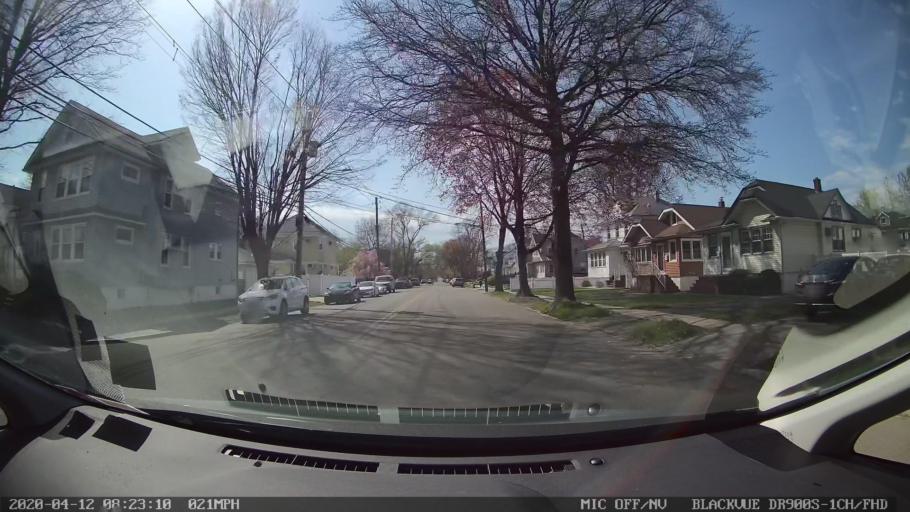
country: US
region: New York
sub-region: Richmond County
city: Bloomfield
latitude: 40.6215
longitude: -74.1359
